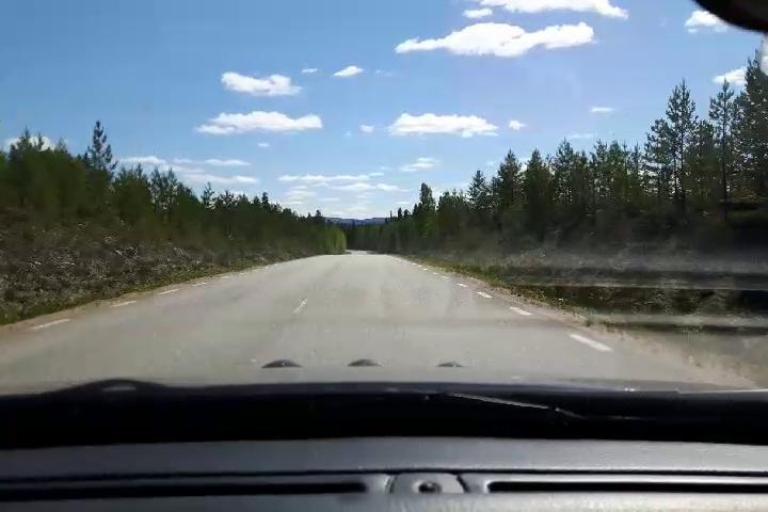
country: SE
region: Gaevleborg
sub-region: Ljusdals Kommun
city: Farila
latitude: 61.9997
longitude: 15.2411
